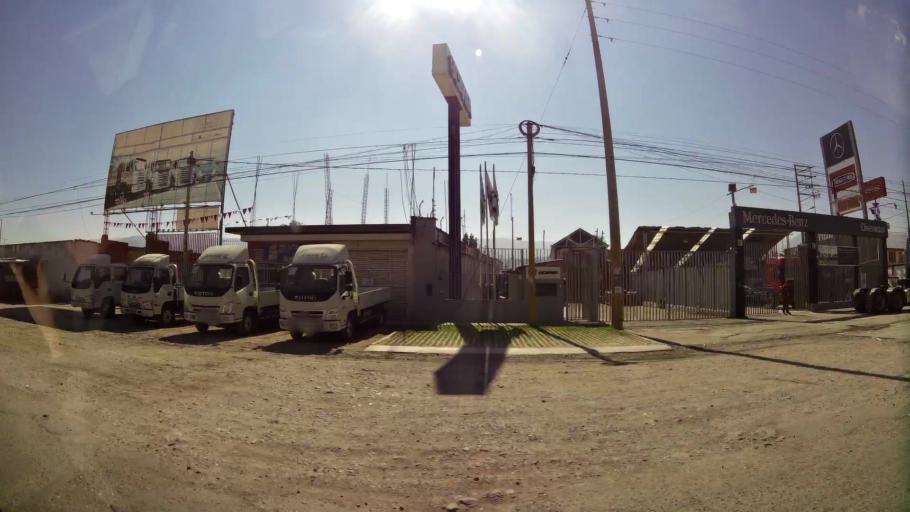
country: PE
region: Junin
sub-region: Provincia de Huancayo
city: Pilcomay
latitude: -12.0251
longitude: -75.2379
